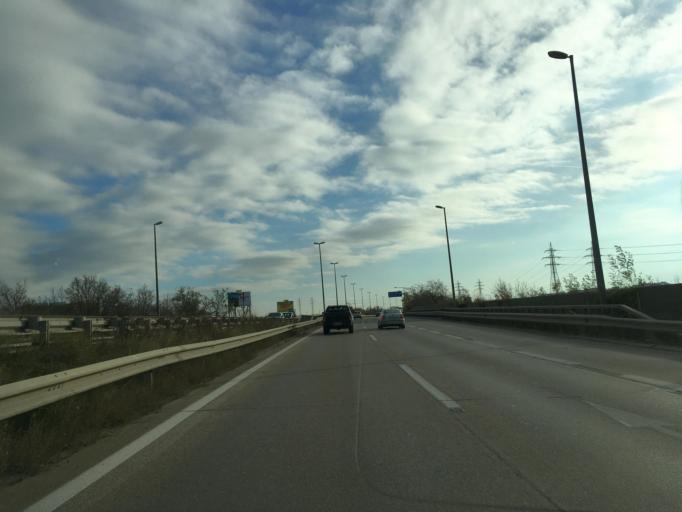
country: AT
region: Lower Austria
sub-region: Politischer Bezirk Wien-Umgebung
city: Schwechat
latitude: 48.1624
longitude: 16.4811
